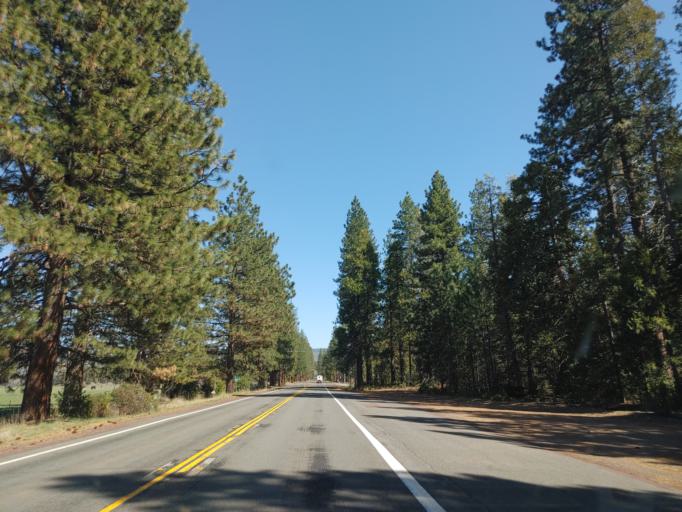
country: US
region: California
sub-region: Shasta County
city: Burney
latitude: 40.7423
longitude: -121.4718
